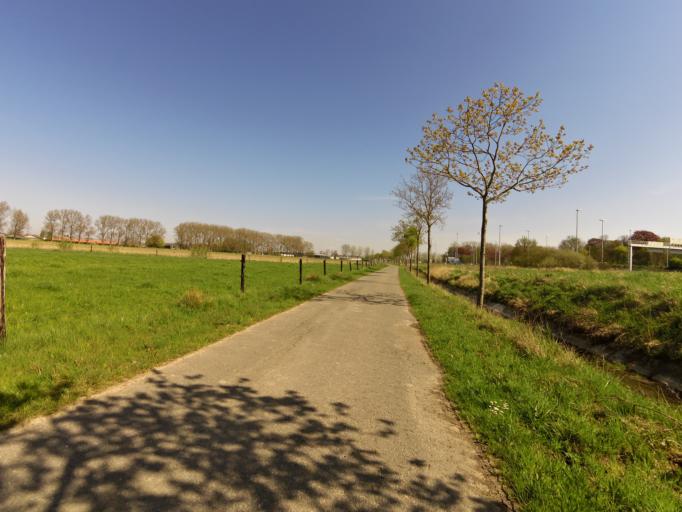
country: BE
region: Flanders
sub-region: Provincie West-Vlaanderen
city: Jabbeke
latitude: 51.1939
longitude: 3.0816
